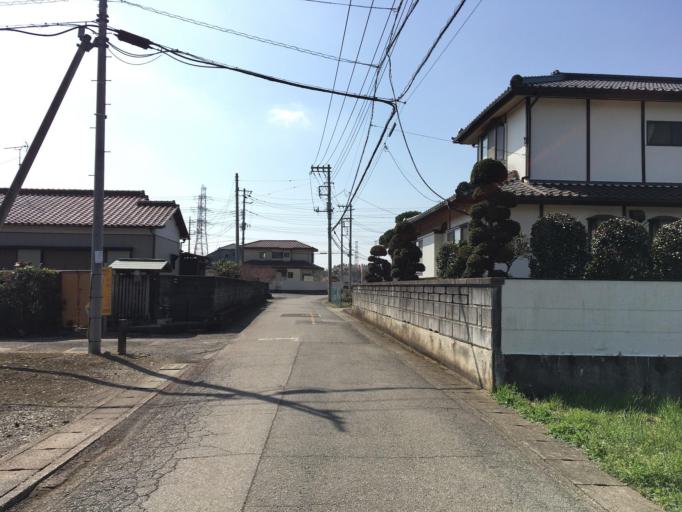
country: JP
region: Saitama
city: Sakado
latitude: 35.9283
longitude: 139.3572
